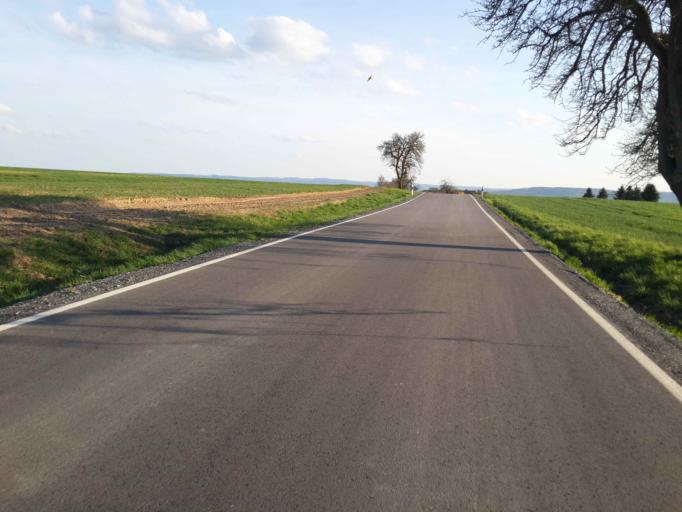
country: DE
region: Baden-Wuerttemberg
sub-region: Regierungsbezirk Stuttgart
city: Widdern
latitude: 49.2725
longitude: 9.4209
